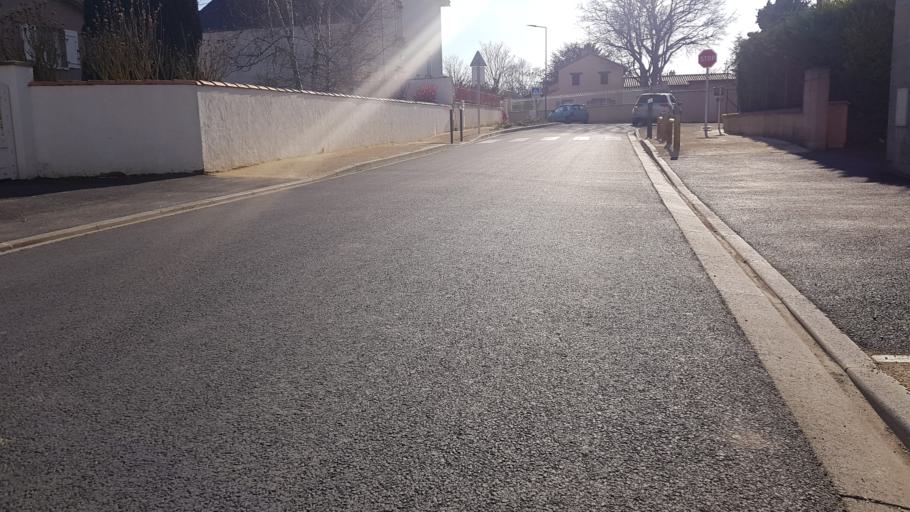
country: FR
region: Poitou-Charentes
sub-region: Departement de la Vienne
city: Avanton
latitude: 46.6609
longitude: 0.3056
